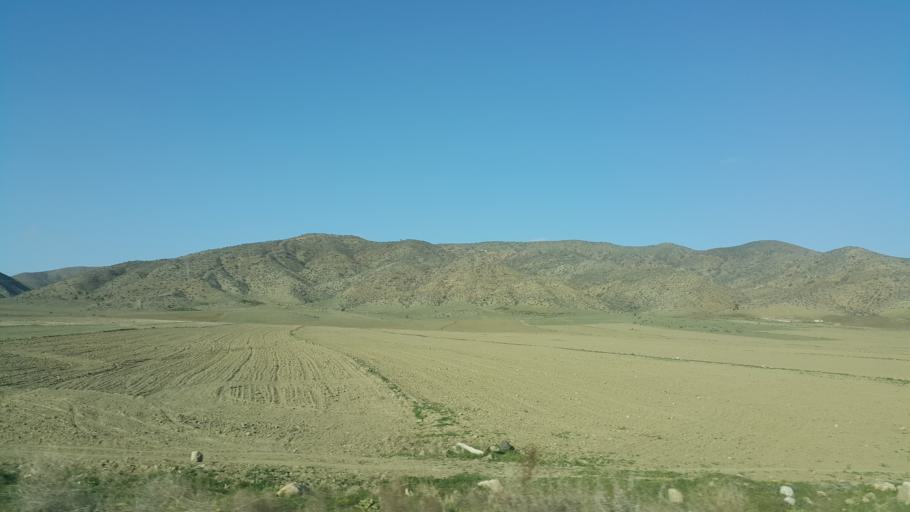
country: TR
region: Ankara
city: Sereflikochisar
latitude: 38.7973
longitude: 33.6224
